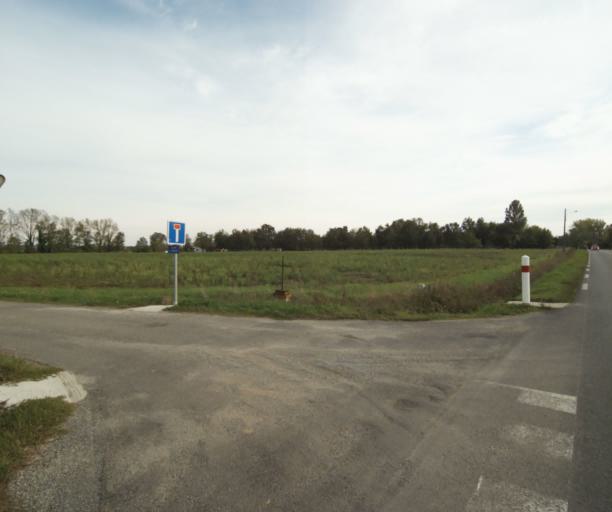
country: FR
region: Midi-Pyrenees
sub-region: Departement du Tarn-et-Garonne
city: Labastide-Saint-Pierre
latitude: 43.9281
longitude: 1.3618
